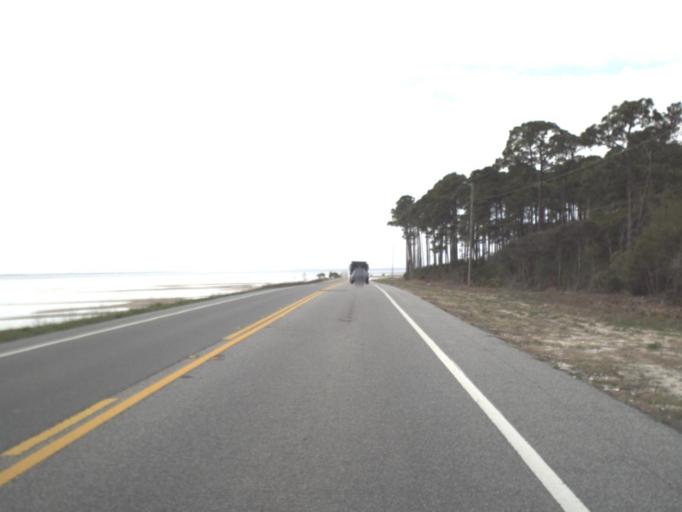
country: US
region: Florida
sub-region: Franklin County
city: Eastpoint
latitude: 29.7712
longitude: -84.7957
